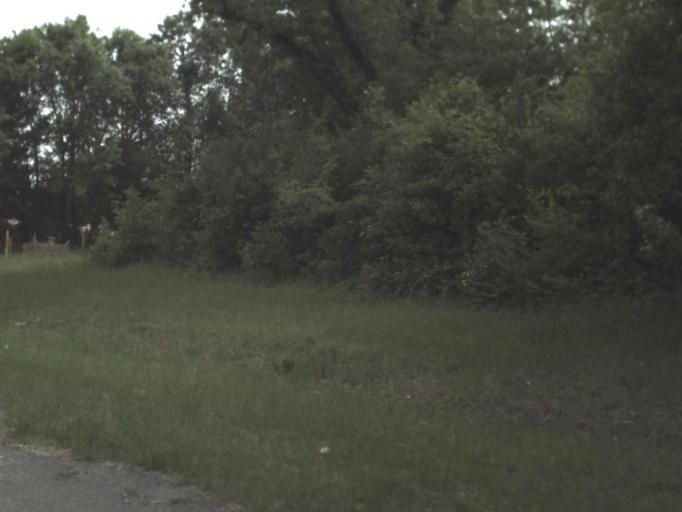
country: US
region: Alabama
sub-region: Escambia County
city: East Brewton
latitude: 30.9997
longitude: -87.0365
